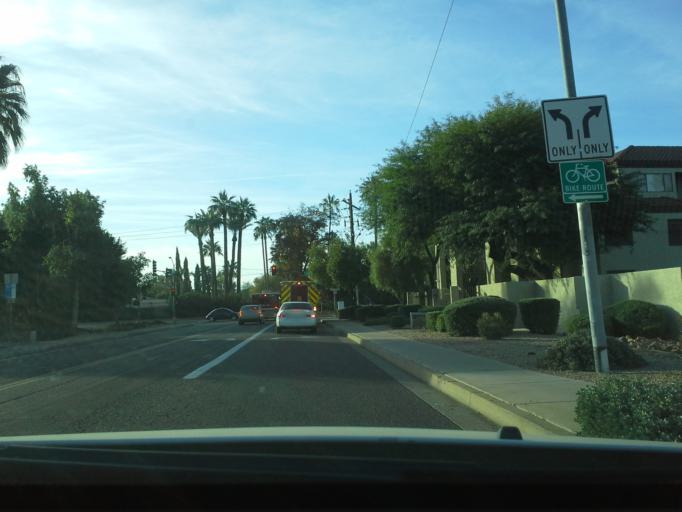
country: US
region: Arizona
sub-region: Maricopa County
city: Phoenix
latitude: 33.4882
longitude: -112.0564
